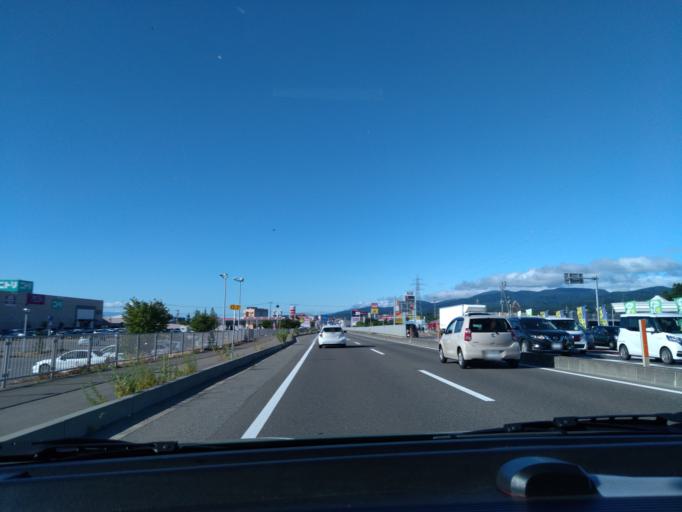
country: JP
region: Akita
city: Yokotemachi
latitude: 39.2970
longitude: 140.5546
